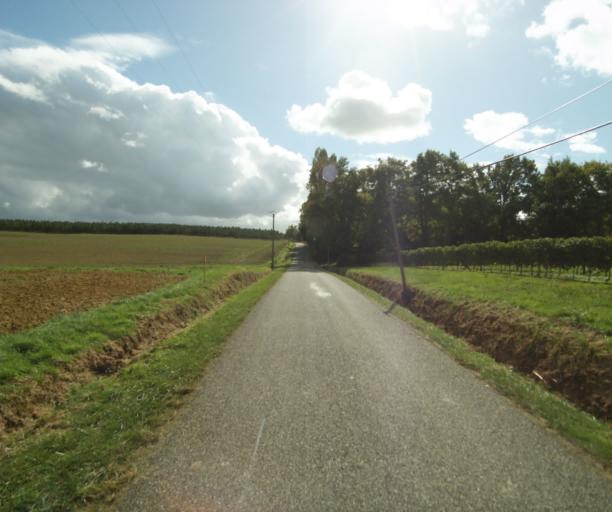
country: FR
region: Midi-Pyrenees
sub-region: Departement du Gers
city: Cazaubon
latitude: 43.8578
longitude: -0.0191
